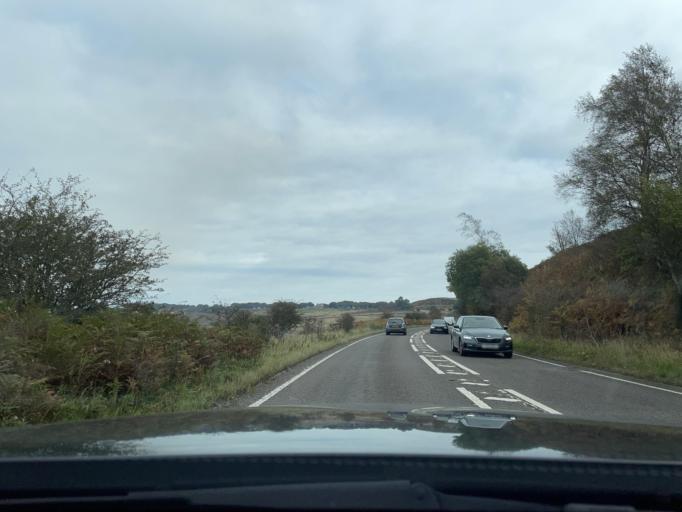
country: GB
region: England
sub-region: Derbyshire
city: Hathersage
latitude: 53.3850
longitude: -1.6692
